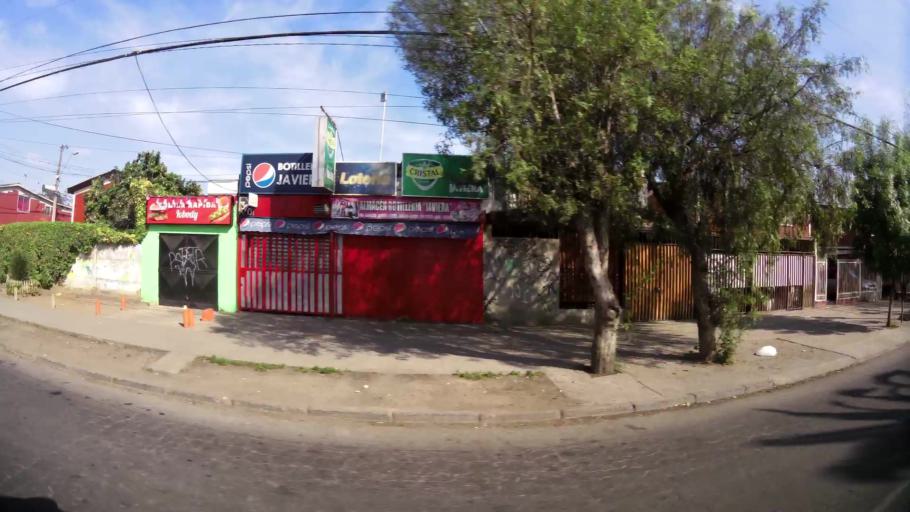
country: CL
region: Santiago Metropolitan
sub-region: Provincia de Santiago
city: Lo Prado
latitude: -33.4581
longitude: -70.7517
